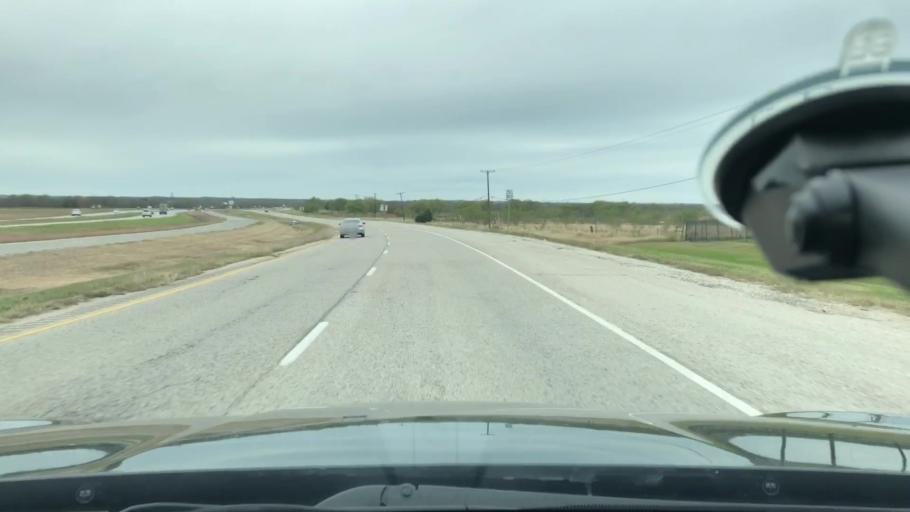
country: US
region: Texas
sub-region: Kaufman County
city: Talty
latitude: 32.7407
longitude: -96.3622
